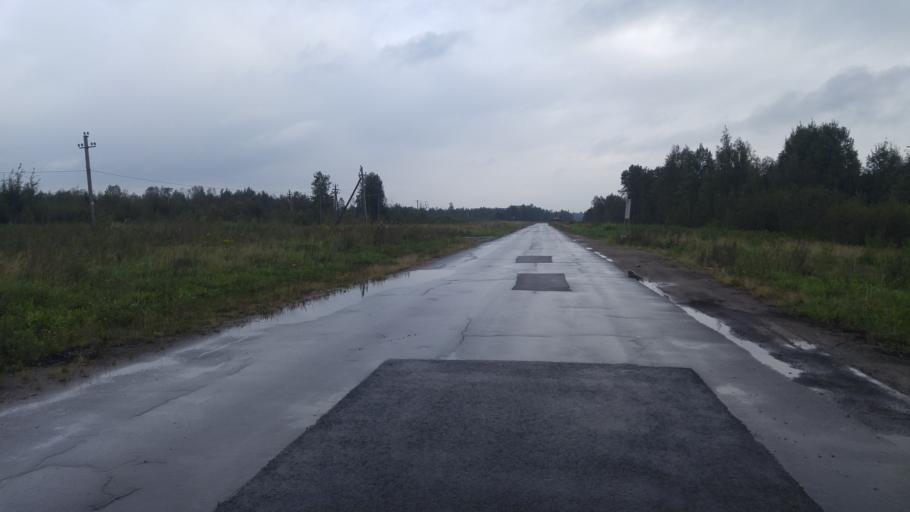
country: RU
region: St.-Petersburg
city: Metallostroy
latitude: 59.7818
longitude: 30.5715
